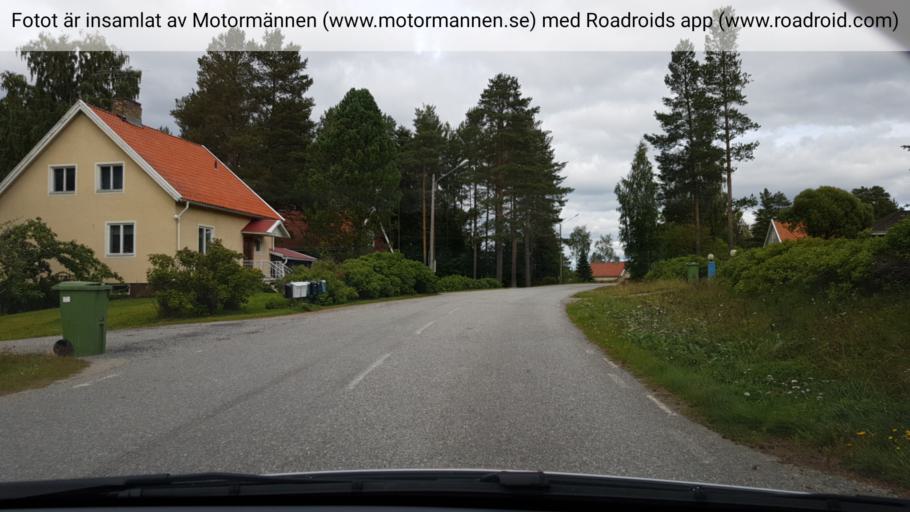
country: SE
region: Vaesterbotten
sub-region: Vannas Kommun
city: Vannasby
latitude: 64.0865
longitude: 19.9497
